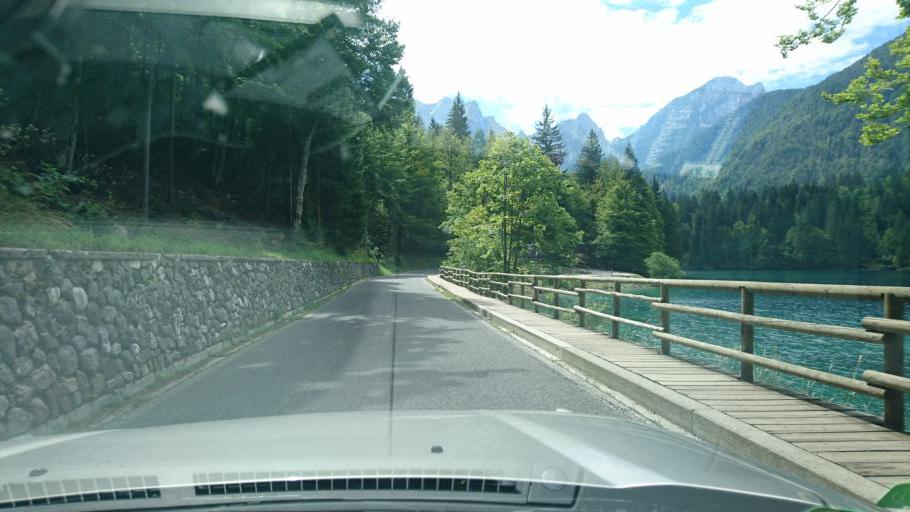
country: AT
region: Carinthia
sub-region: Politischer Bezirk Villach Land
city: Arnoldstein
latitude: 46.4819
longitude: 13.6747
